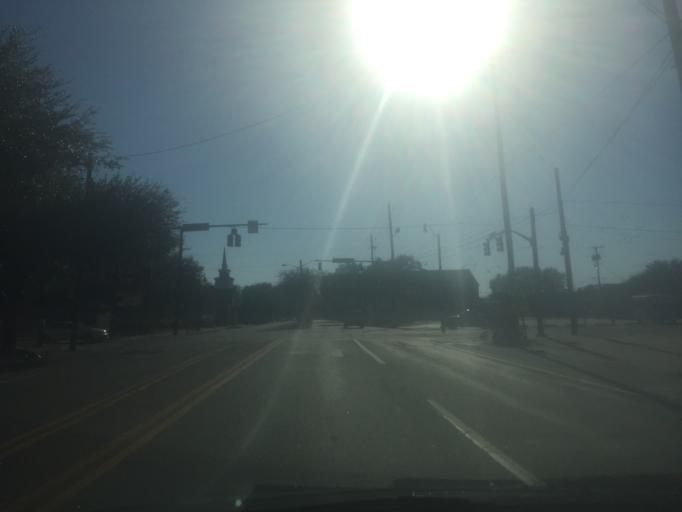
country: US
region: Georgia
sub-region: Chatham County
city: Savannah
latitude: 32.0690
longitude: -81.1015
